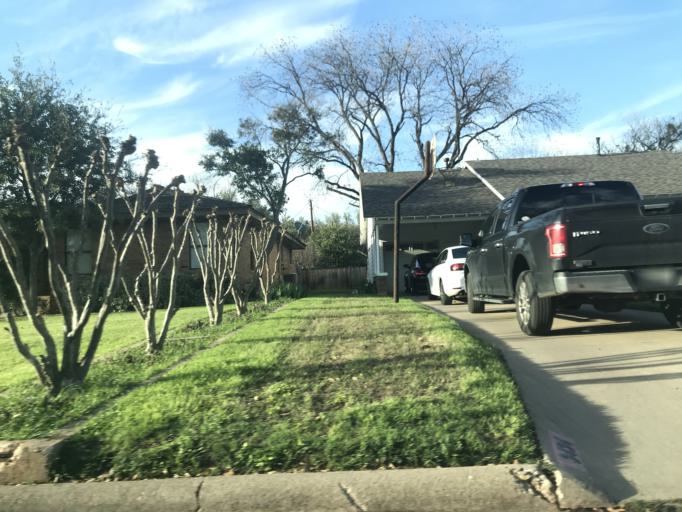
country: US
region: Texas
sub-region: Taylor County
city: Abilene
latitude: 32.4340
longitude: -99.7676
